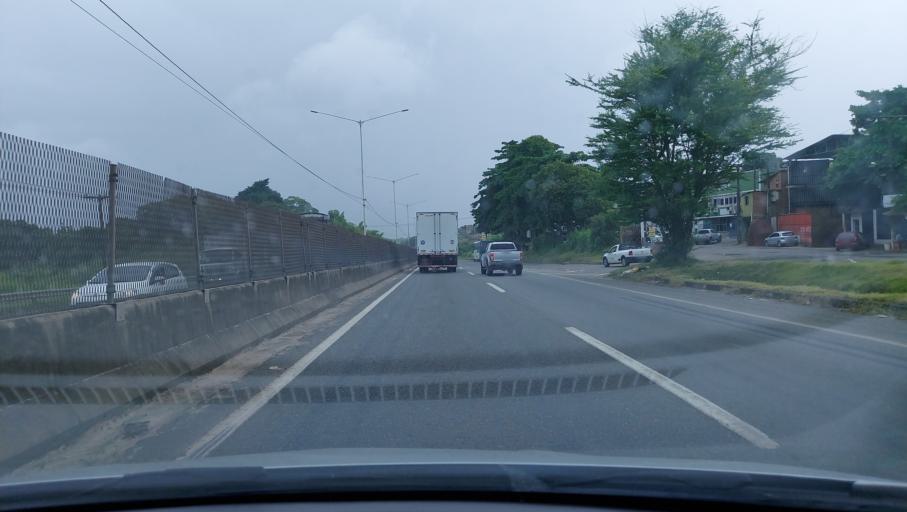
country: BR
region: Bahia
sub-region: Simoes Filho
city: Simoes Filho
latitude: -12.8873
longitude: -38.4398
